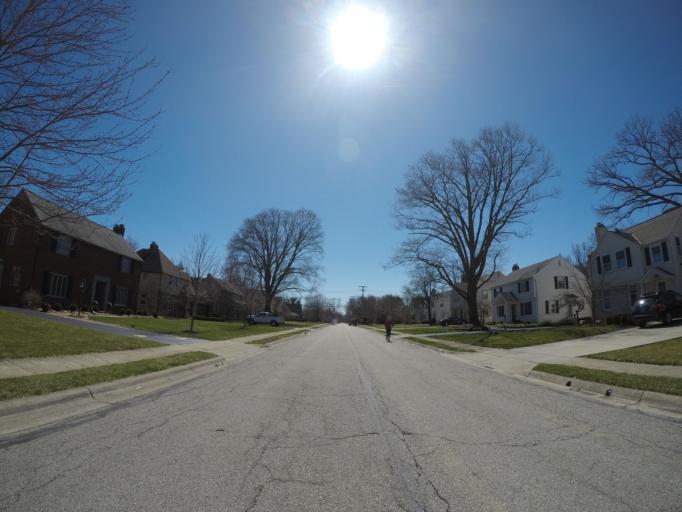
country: US
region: Ohio
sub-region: Franklin County
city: Upper Arlington
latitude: 40.0089
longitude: -83.0603
